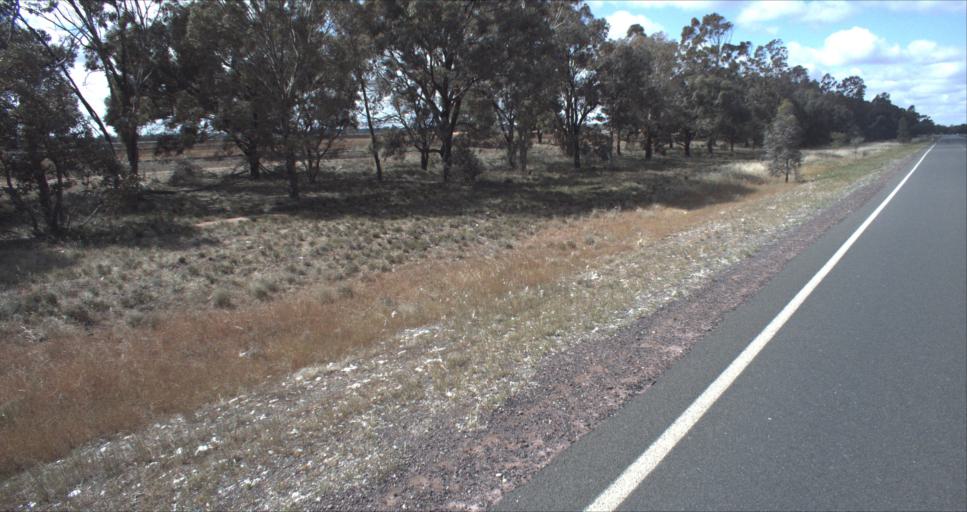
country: AU
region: New South Wales
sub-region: Murrumbidgee Shire
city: Darlington Point
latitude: -34.5878
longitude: 146.1640
